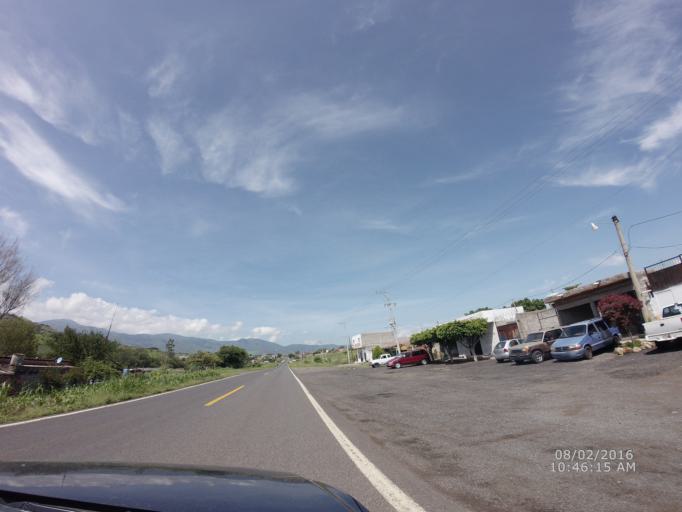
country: MX
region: Nayarit
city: Ixtlan del Rio
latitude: 21.0341
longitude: -104.3474
